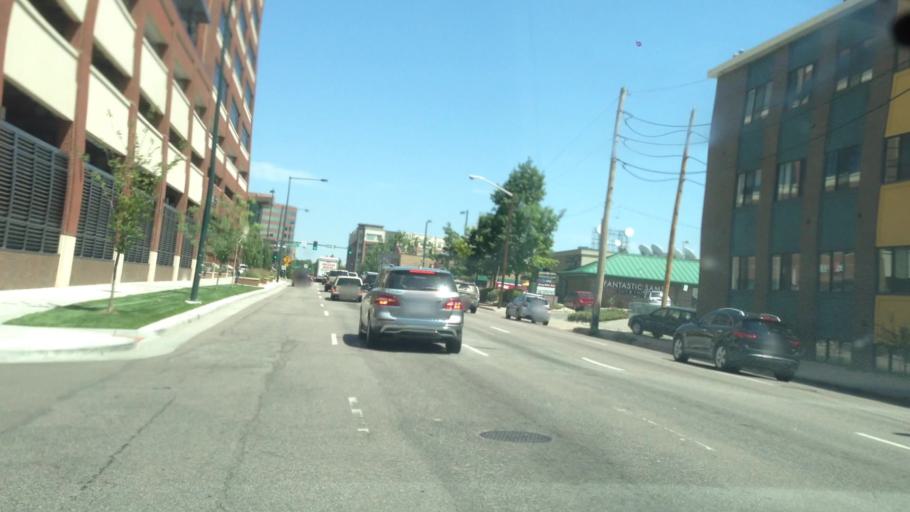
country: US
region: Colorado
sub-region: Denver County
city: Denver
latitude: 39.7257
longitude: -104.9889
